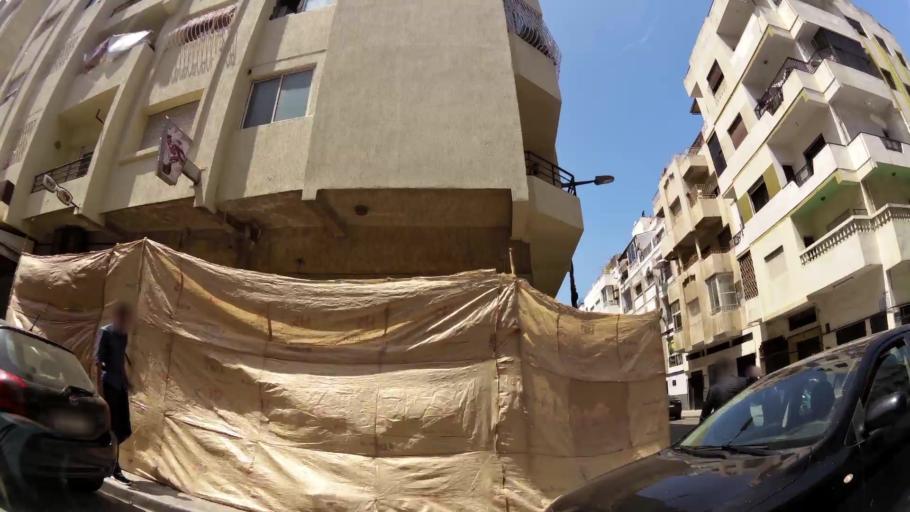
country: MA
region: Rabat-Sale-Zemmour-Zaer
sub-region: Rabat
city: Rabat
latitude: 34.0201
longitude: -6.8508
